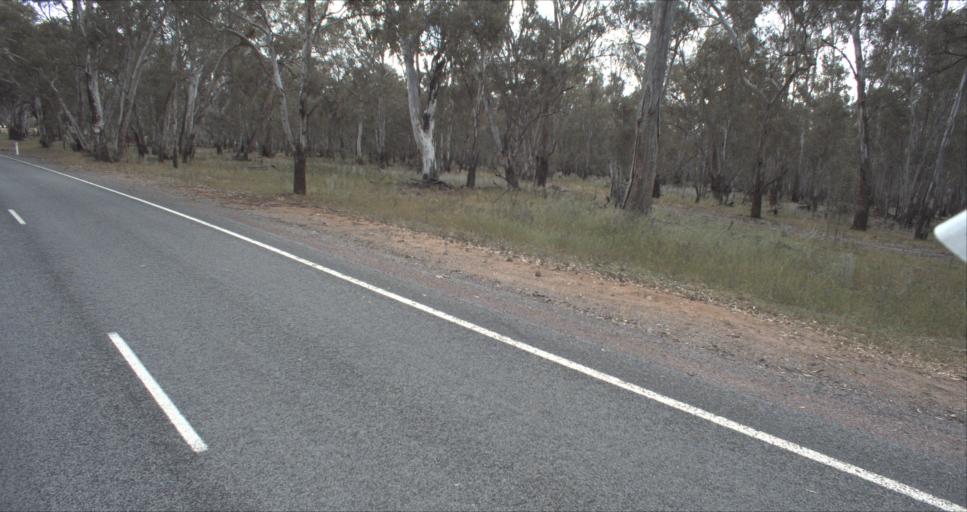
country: AU
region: New South Wales
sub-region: Leeton
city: Leeton
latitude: -34.6414
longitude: 146.3588
